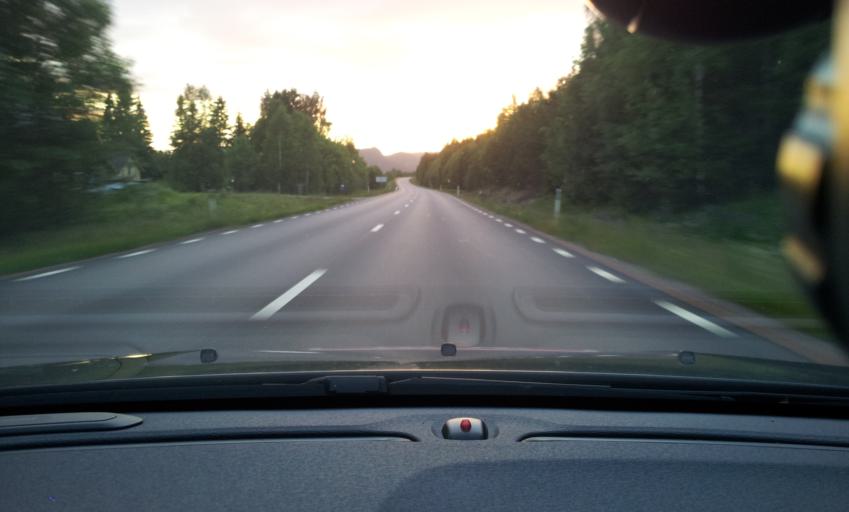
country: SE
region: Jaemtland
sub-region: Ragunda Kommun
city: Hammarstrand
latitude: 63.0662
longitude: 16.5075
